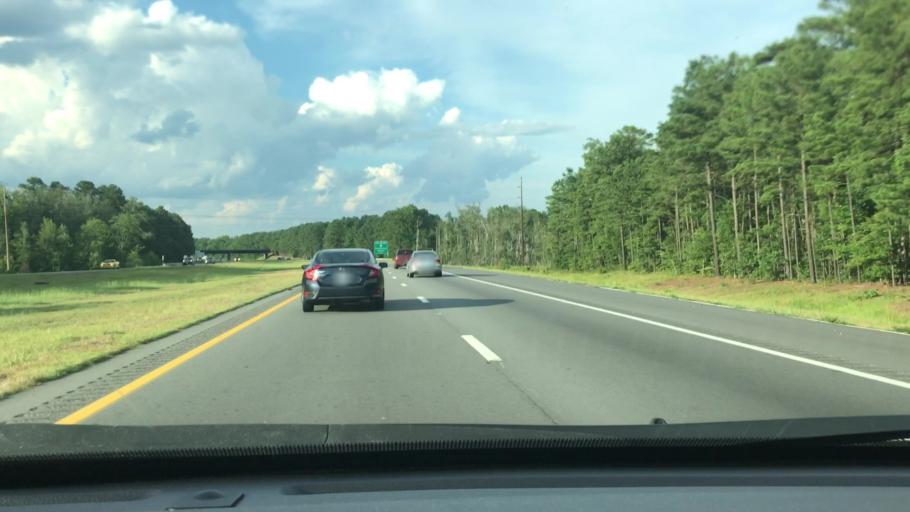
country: US
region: North Carolina
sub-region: Cumberland County
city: Vander
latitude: 35.0190
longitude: -78.8126
